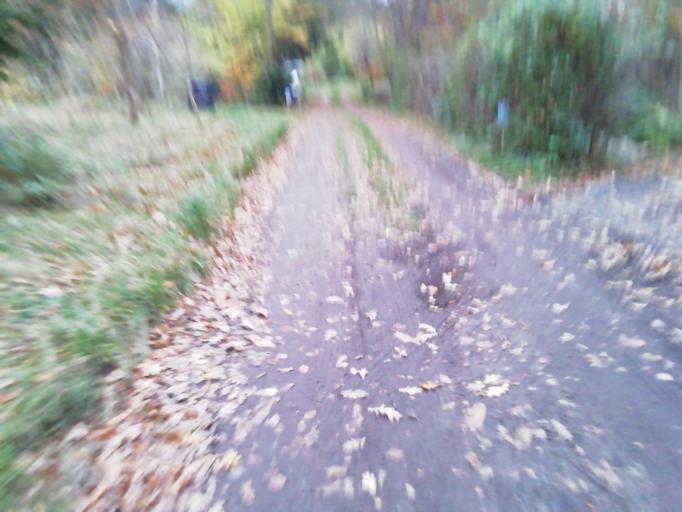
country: DK
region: Capital Region
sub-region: Frederikssund Kommune
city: Jaegerspris
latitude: 55.9031
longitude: 11.9228
